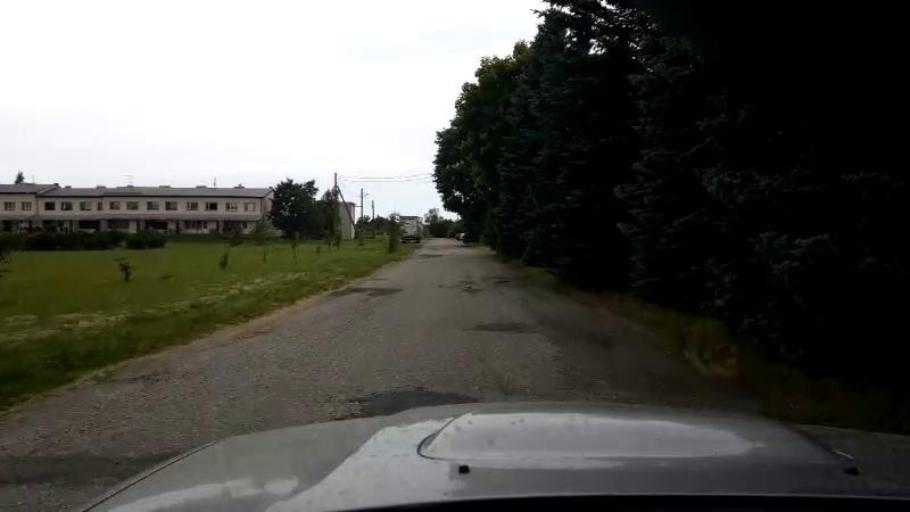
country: EE
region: Paernumaa
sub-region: Tootsi vald
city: Tootsi
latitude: 58.5282
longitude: 24.7016
